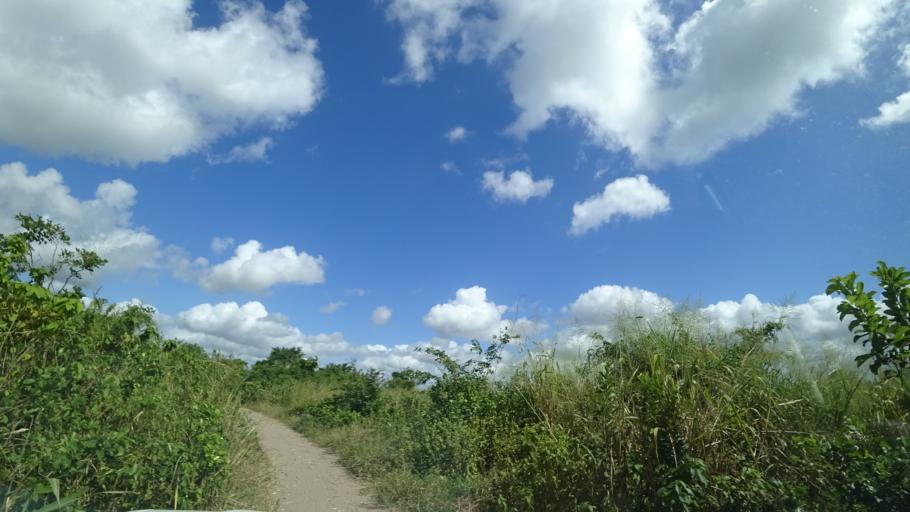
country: MZ
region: Sofala
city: Dondo
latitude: -19.3571
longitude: 34.5798
